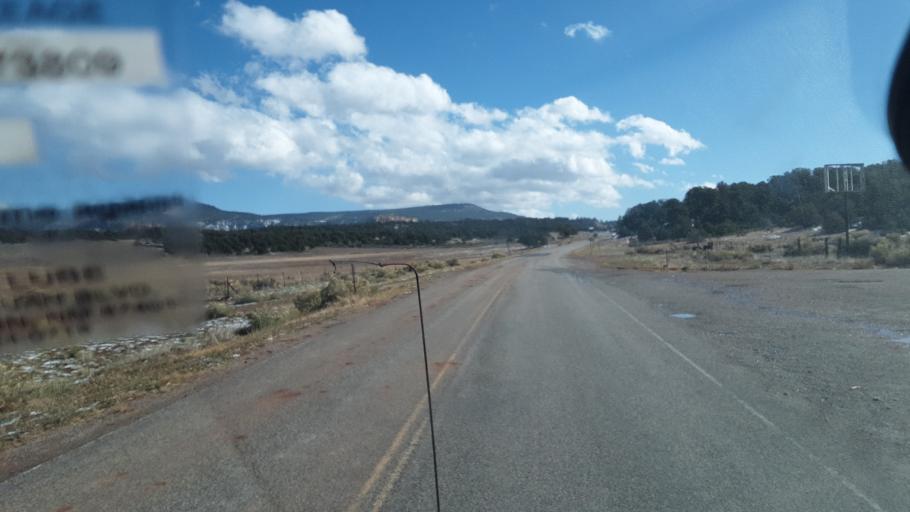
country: US
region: New Mexico
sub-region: Rio Arriba County
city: Santa Teresa
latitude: 36.2355
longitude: -106.8448
